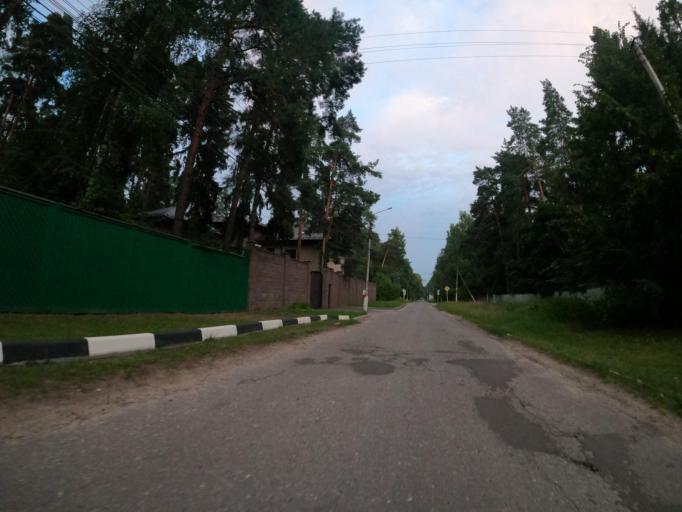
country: RU
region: Moskovskaya
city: Bykovo
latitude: 55.6295
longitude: 38.0980
